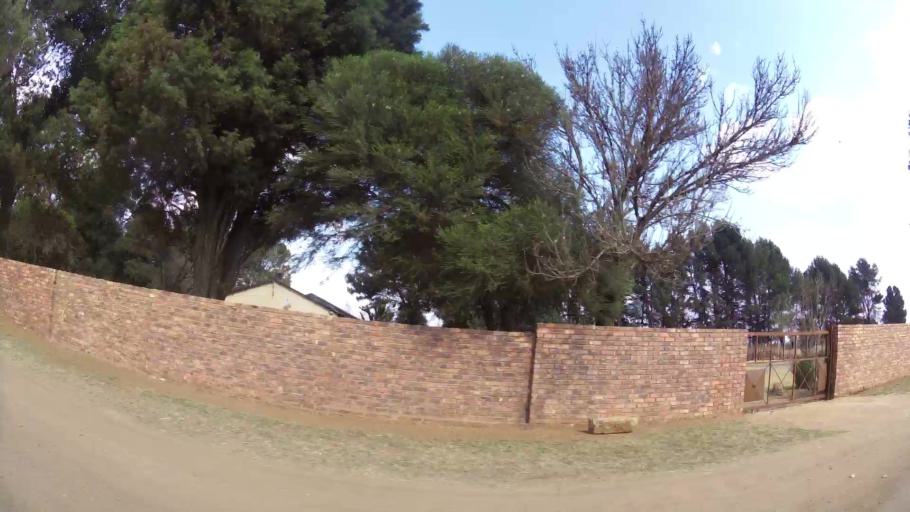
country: ZA
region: Mpumalanga
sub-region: Nkangala District Municipality
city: Delmas
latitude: -26.1487
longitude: 28.5536
